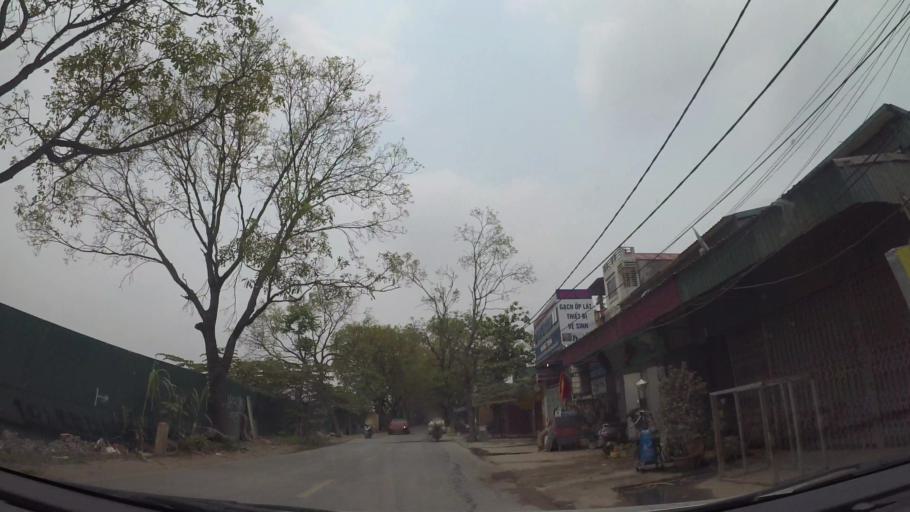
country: VN
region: Ha Noi
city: Cau Dien
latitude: 21.0198
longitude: 105.7439
